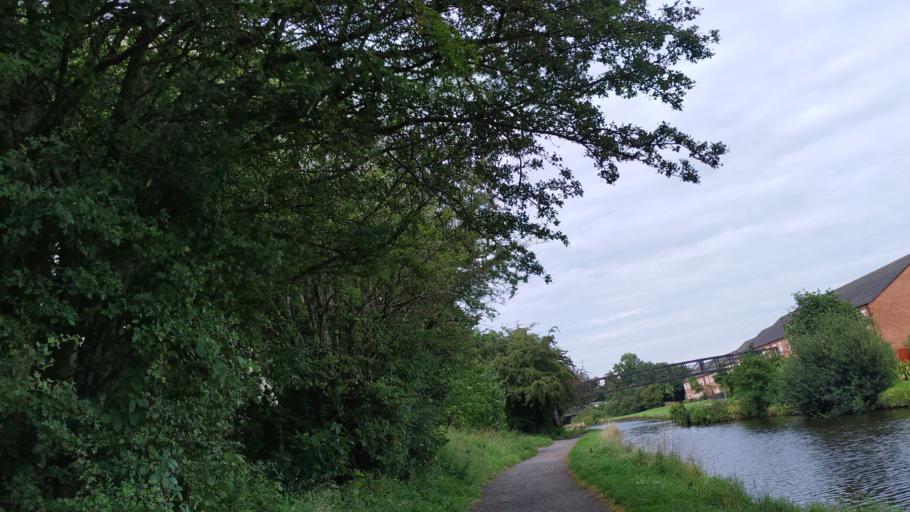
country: GB
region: England
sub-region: Lancashire
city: Chorley
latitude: 53.6542
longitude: -2.6139
